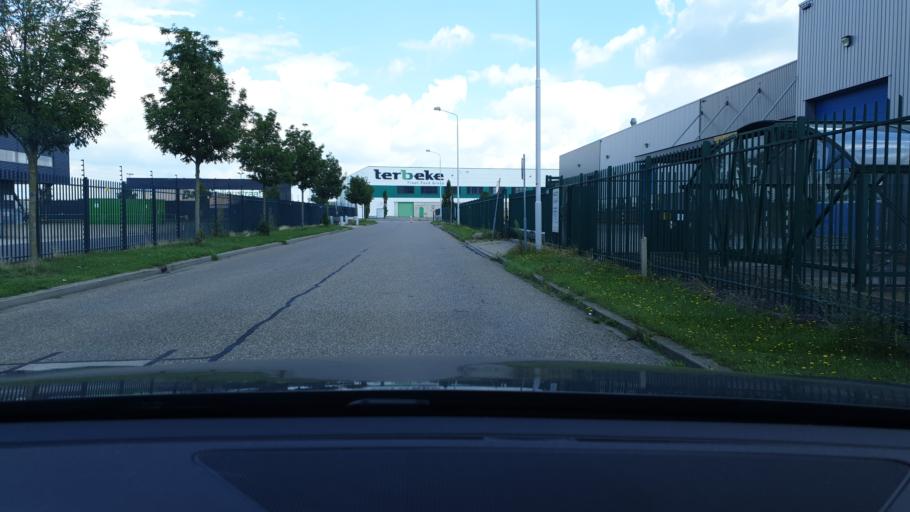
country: NL
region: Gelderland
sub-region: Gemeente Wijchen
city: Wijchen
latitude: 51.8314
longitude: 5.7491
